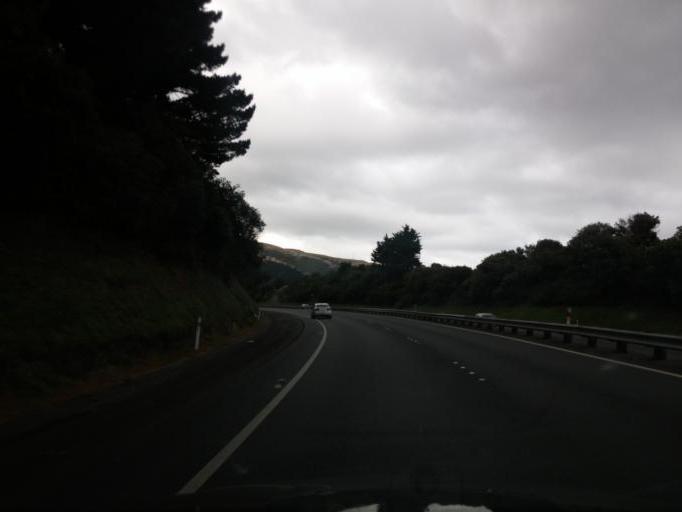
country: NZ
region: Wellington
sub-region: Porirua City
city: Porirua
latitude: -41.1810
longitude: 174.8289
